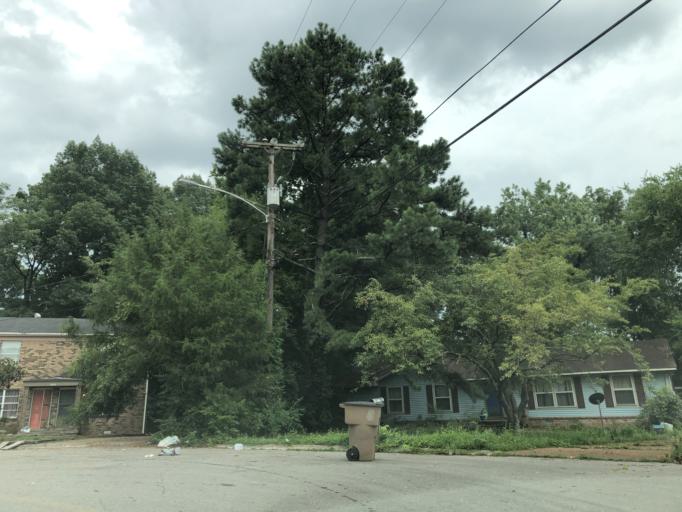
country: US
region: Tennessee
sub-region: Williamson County
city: Brentwood Estates
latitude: 36.0538
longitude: -86.6886
